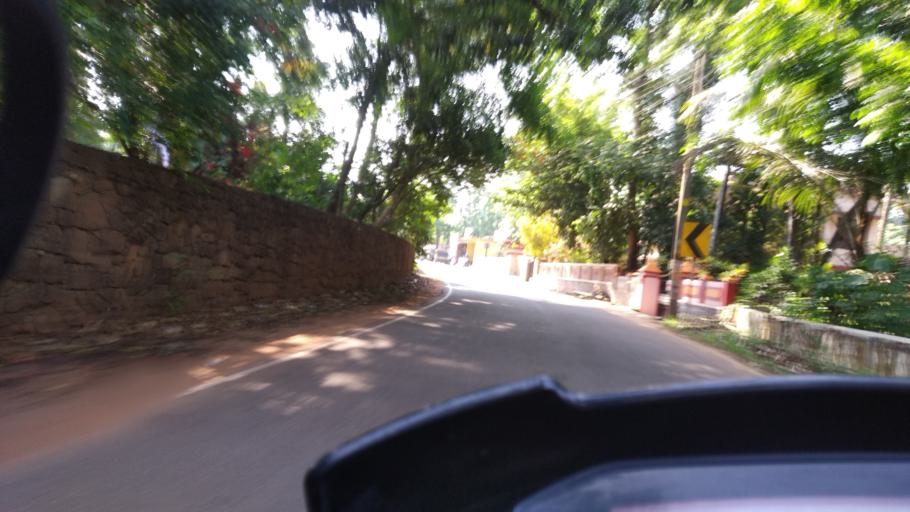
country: IN
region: Kerala
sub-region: Ernakulam
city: Piravam
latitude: 9.8613
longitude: 76.5176
